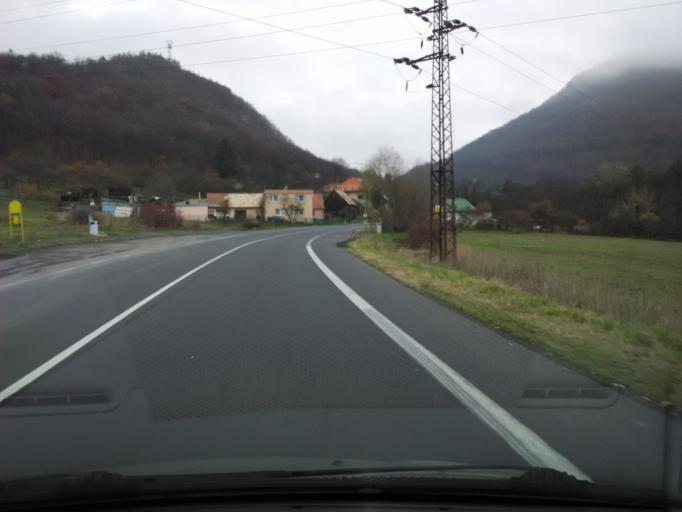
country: SK
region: Banskobystricky
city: Ziar nad Hronom
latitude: 48.5907
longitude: 18.8951
